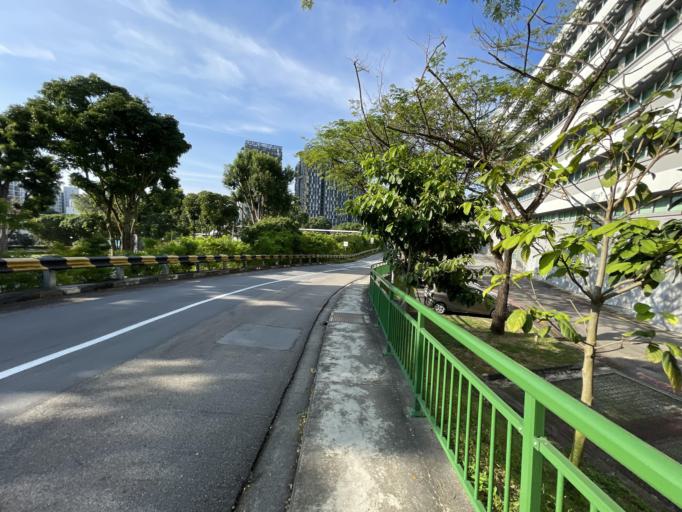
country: SG
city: Singapore
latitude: 1.2998
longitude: 103.7702
